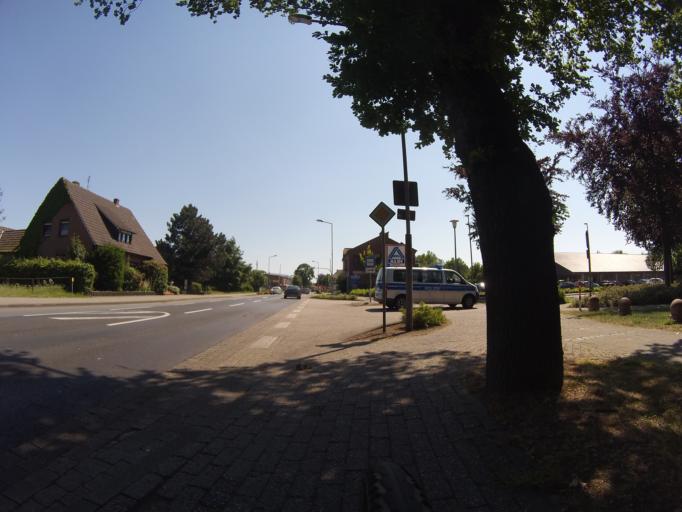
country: DE
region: Lower Saxony
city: Emlichheim
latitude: 52.6104
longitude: 6.8534
